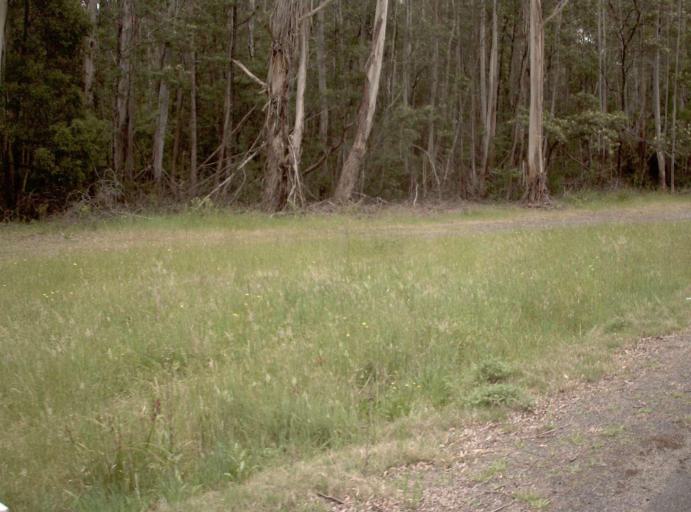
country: AU
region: New South Wales
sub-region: Bombala
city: Bombala
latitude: -37.2823
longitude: 149.2226
